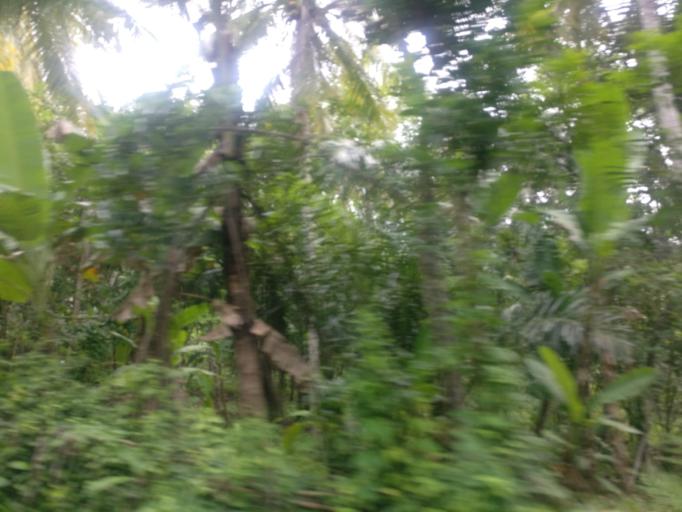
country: ID
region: Bali
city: Banjar Kawan
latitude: -8.4921
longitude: 115.5160
